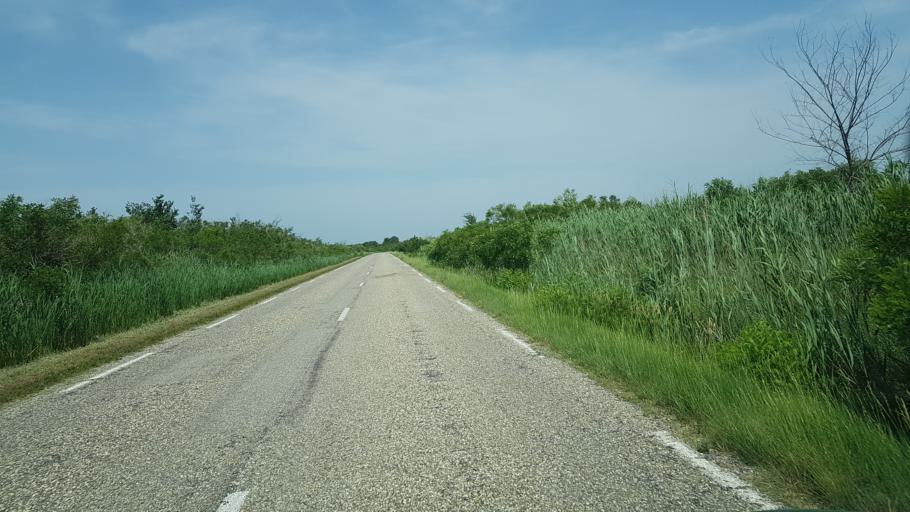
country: FR
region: Languedoc-Roussillon
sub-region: Departement du Gard
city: Saint-Gilles
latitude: 43.5881
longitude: 4.4966
